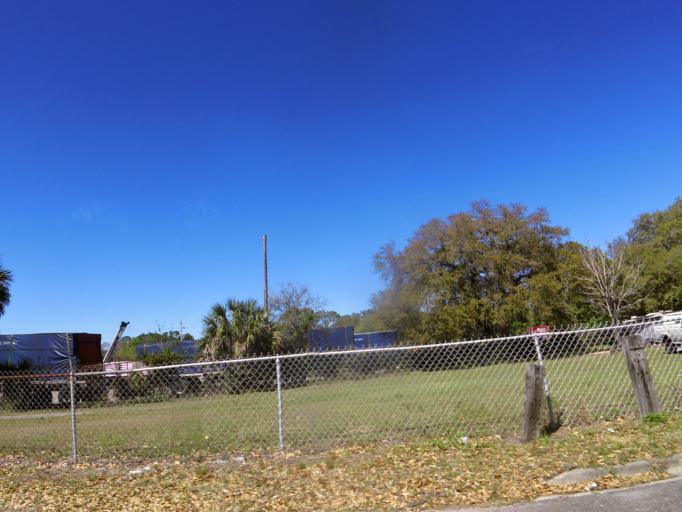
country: US
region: Florida
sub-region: Duval County
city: Jacksonville
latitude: 30.3612
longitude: -81.6407
